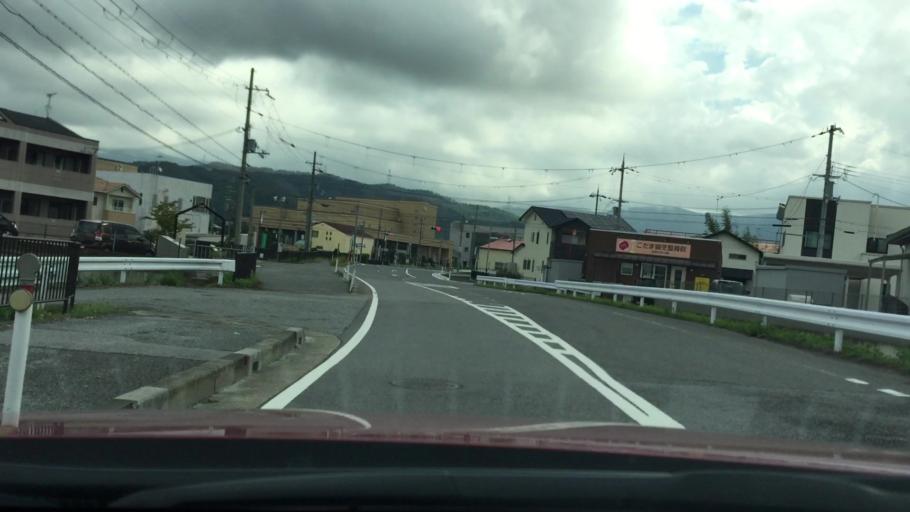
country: JP
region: Shiga Prefecture
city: Nagahama
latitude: 35.4267
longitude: 136.2968
